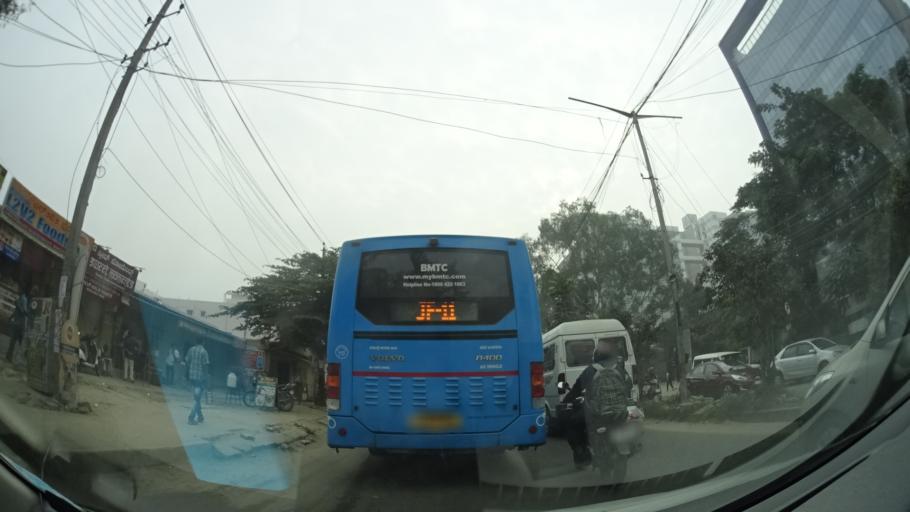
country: IN
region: Karnataka
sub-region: Bangalore Urban
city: Bangalore
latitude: 12.9938
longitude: 77.7024
